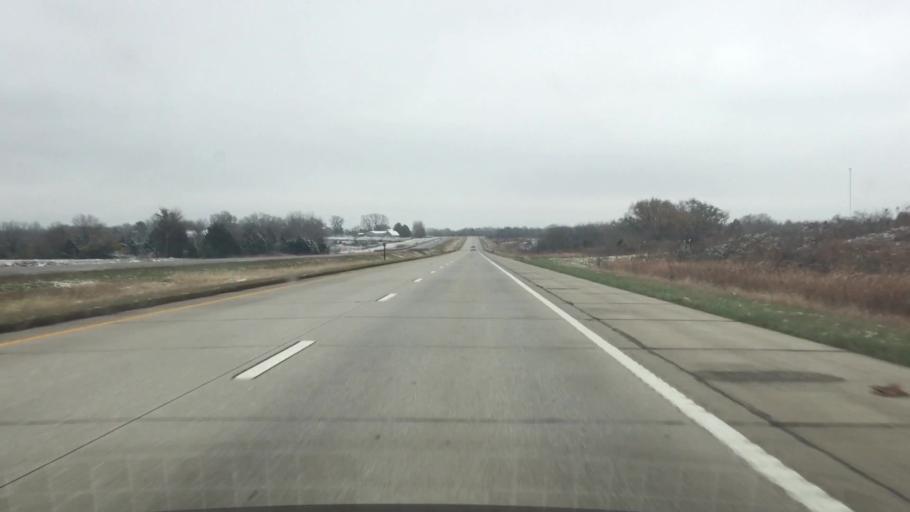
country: US
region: Missouri
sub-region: Saint Clair County
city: Osceola
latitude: 38.1975
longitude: -93.7462
